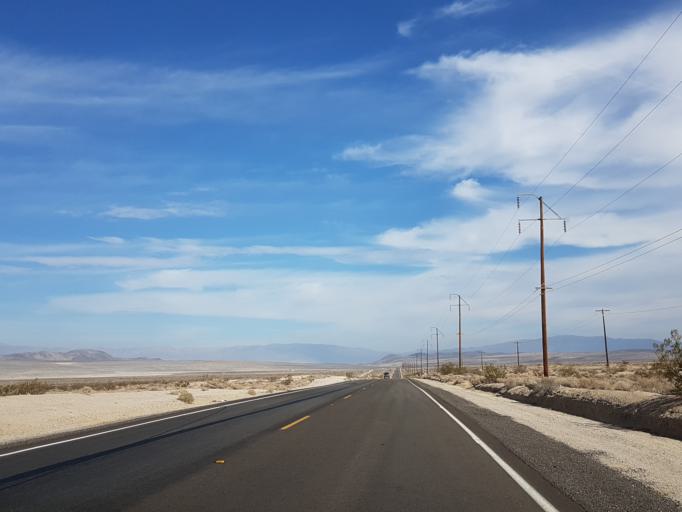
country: US
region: California
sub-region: Kern County
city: Ridgecrest
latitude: 35.6440
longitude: -117.5378
